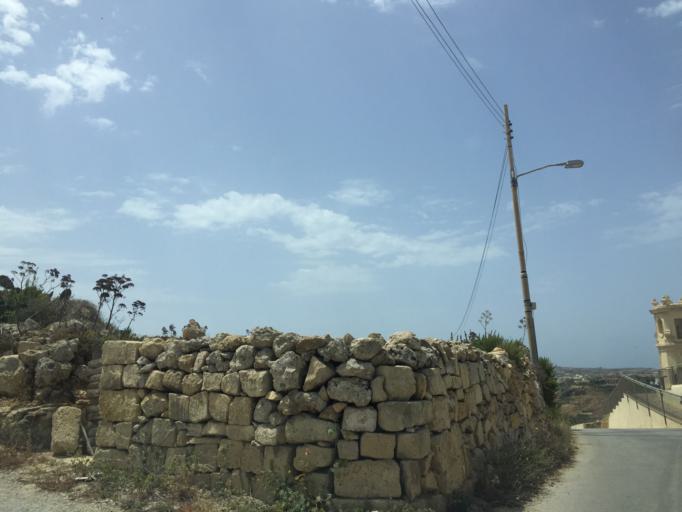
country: MT
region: Ix-Xaghra
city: Xaghra
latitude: 36.0471
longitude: 14.2548
